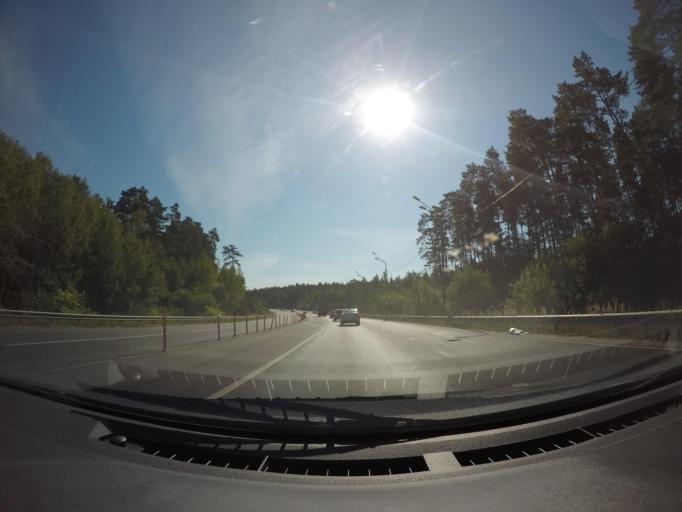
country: RU
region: Moskovskaya
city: Kratovo
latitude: 55.6366
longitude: 38.1876
